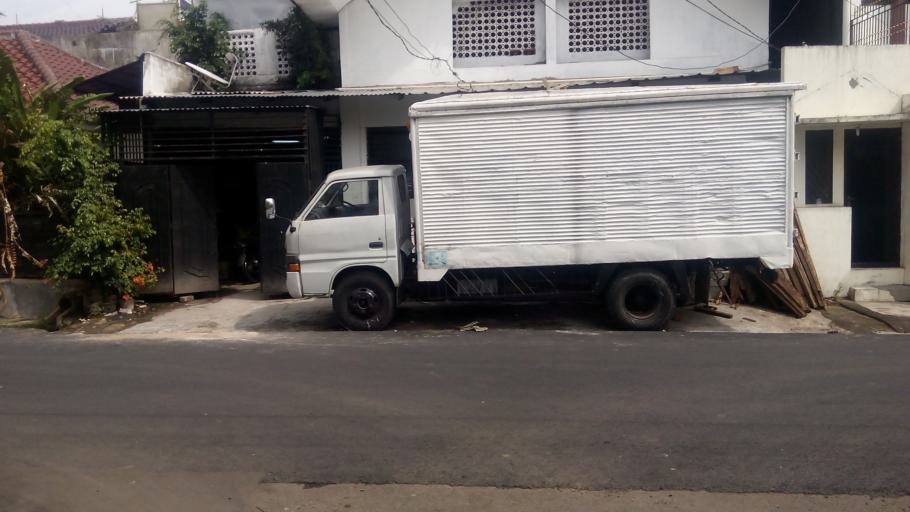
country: ID
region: Jakarta Raya
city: Jakarta
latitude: -6.2384
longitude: 106.8574
